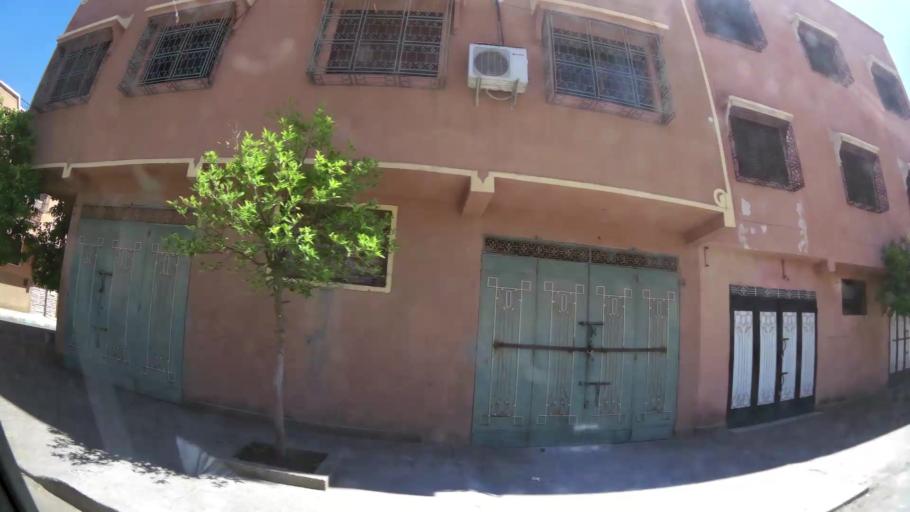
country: MA
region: Marrakech-Tensift-Al Haouz
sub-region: Marrakech
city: Marrakesh
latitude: 31.6551
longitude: -7.9882
